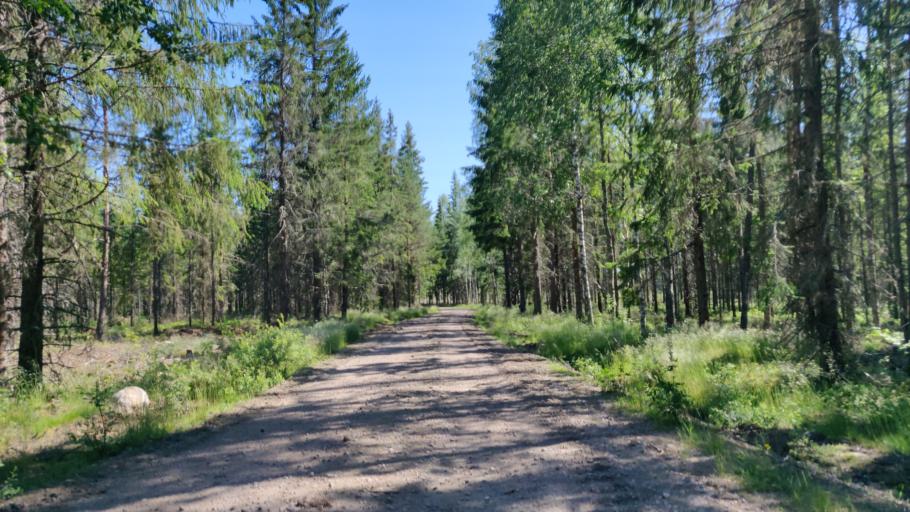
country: SE
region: Vaermland
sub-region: Hagfors Kommun
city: Hagfors
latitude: 59.9752
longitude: 13.6014
